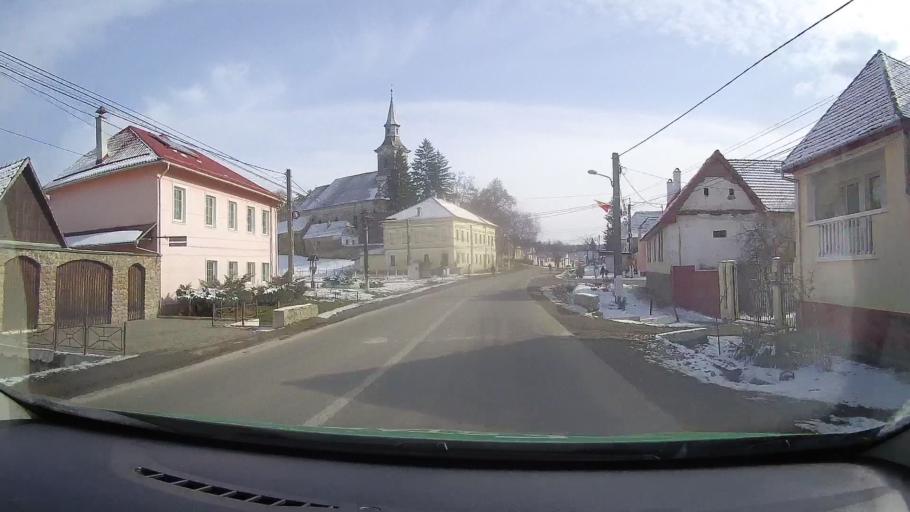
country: RO
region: Mures
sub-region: Comuna Apold
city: Saes
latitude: 46.1563
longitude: 24.7683
